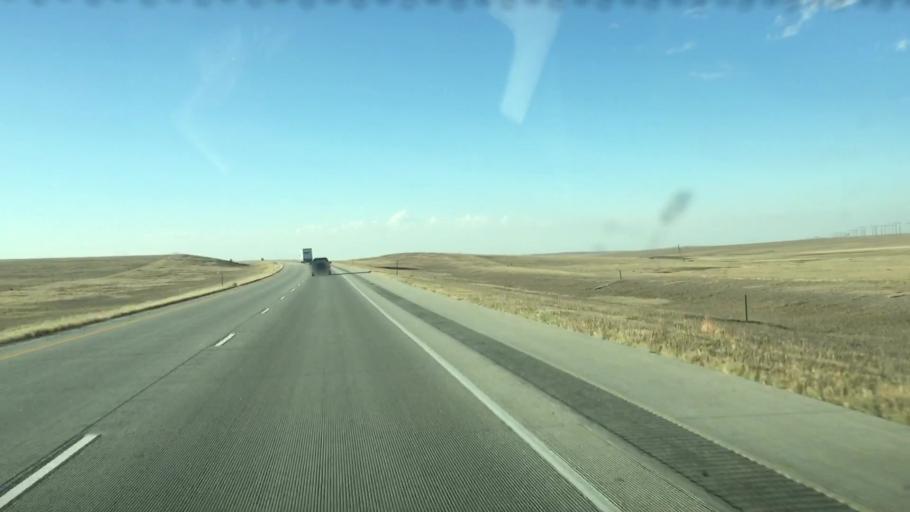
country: US
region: Colorado
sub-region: Lincoln County
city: Limon
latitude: 39.4111
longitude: -103.9003
